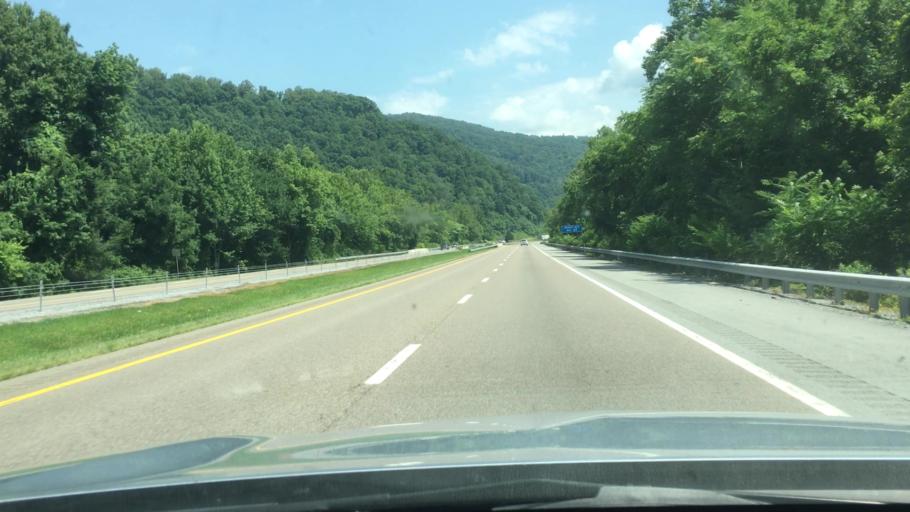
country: US
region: Tennessee
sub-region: Unicoi County
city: Banner Hill
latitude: 36.1407
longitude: -82.4292
